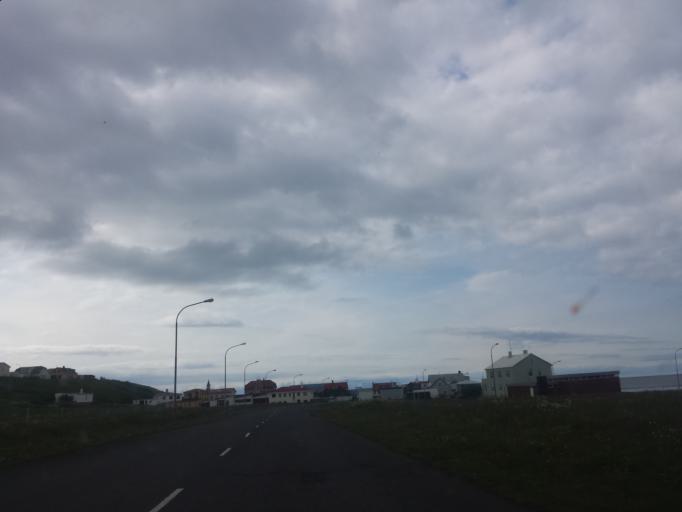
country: IS
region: Northwest
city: Saudarkrokur
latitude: 65.6585
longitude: -20.2958
